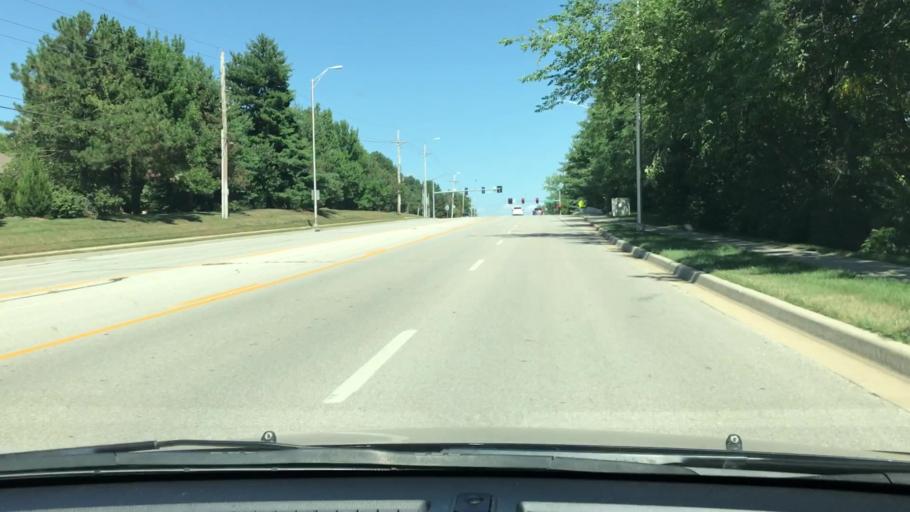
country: US
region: Missouri
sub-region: Jackson County
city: Lees Summit
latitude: 38.9123
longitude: -94.4296
